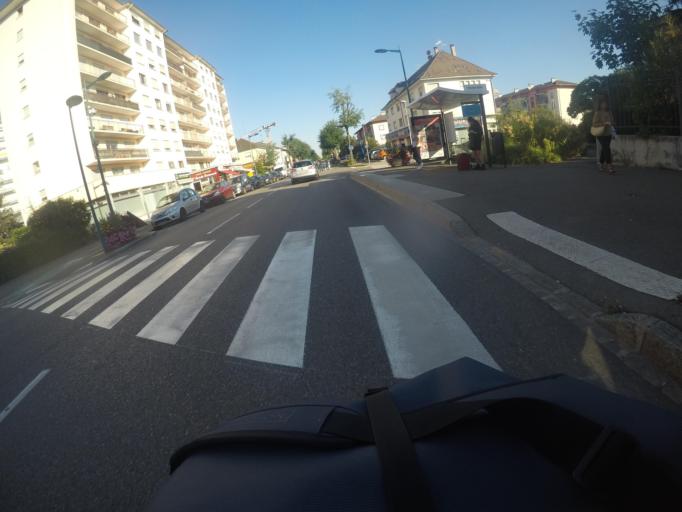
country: FR
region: Alsace
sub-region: Departement du Haut-Rhin
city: Village-Neuf
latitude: 47.5778
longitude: 7.5714
